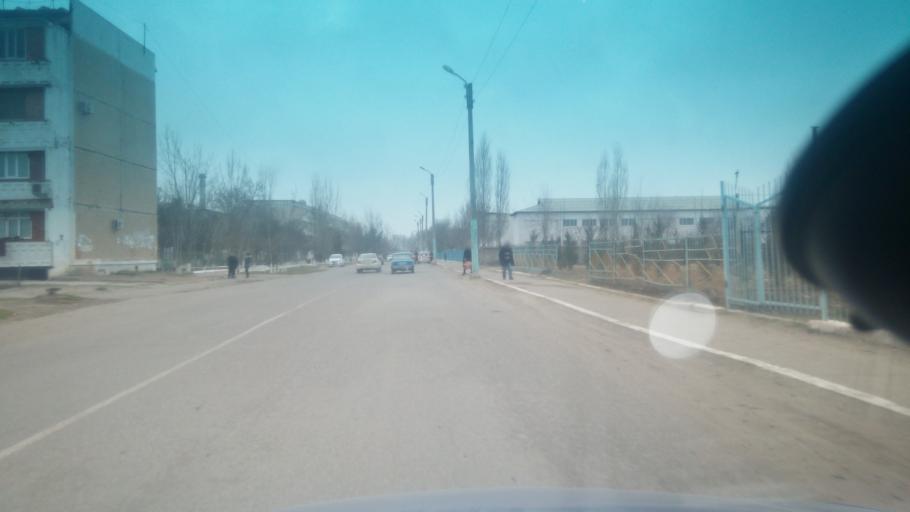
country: UZ
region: Sirdaryo
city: Guliston
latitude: 40.5174
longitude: 68.7783
